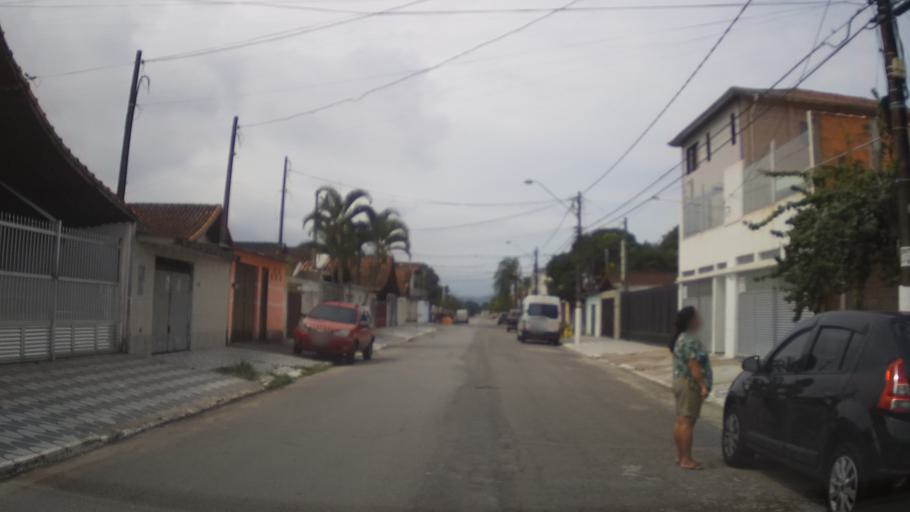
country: BR
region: Sao Paulo
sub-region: Praia Grande
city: Praia Grande
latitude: -24.0166
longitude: -46.4707
